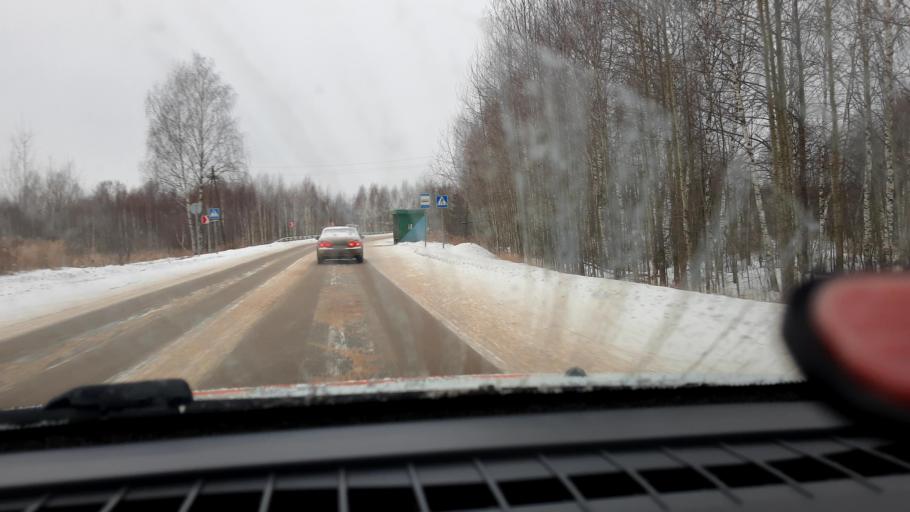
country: RU
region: Nizjnij Novgorod
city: Afonino
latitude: 56.3122
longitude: 44.2250
